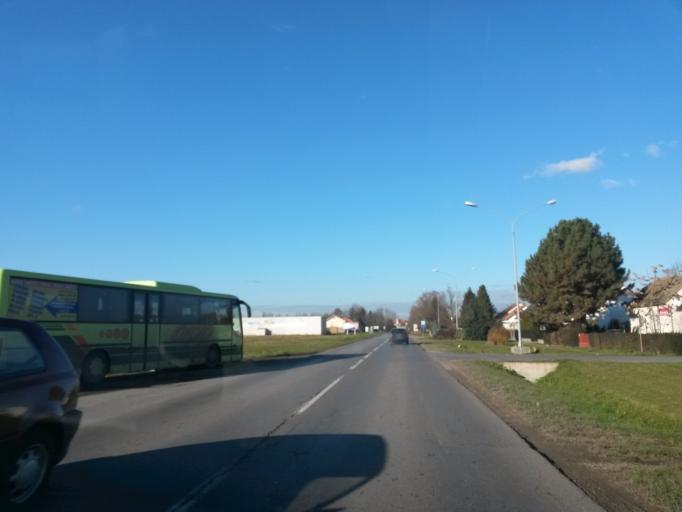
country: HR
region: Osjecko-Baranjska
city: Valpovo
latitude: 45.6528
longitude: 18.4315
